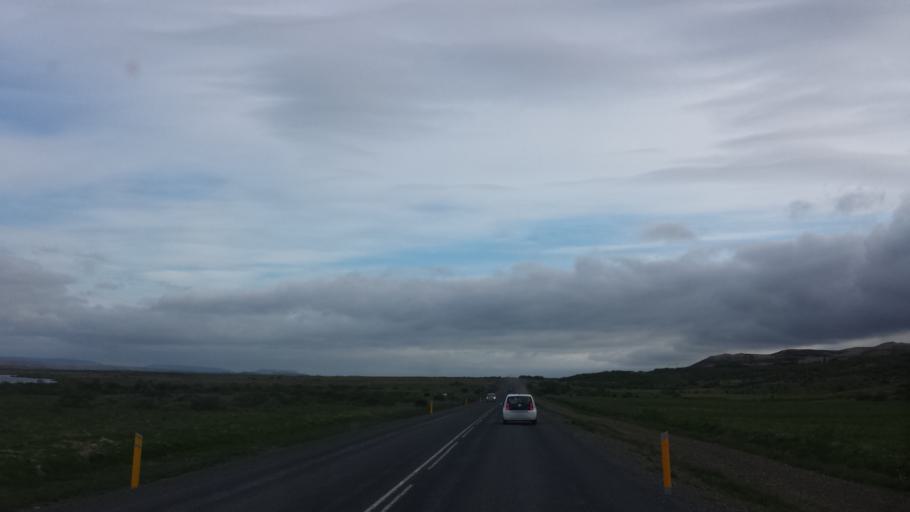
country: IS
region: South
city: Selfoss
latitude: 64.2957
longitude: -20.3343
